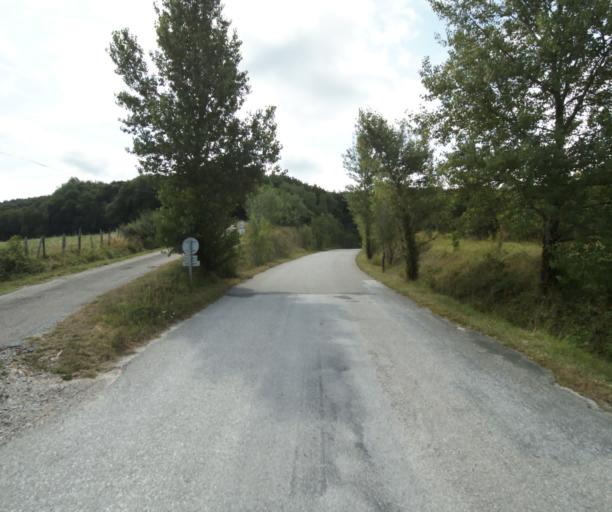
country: FR
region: Midi-Pyrenees
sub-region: Departement du Tarn
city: Dourgne
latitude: 43.4650
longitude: 2.1054
